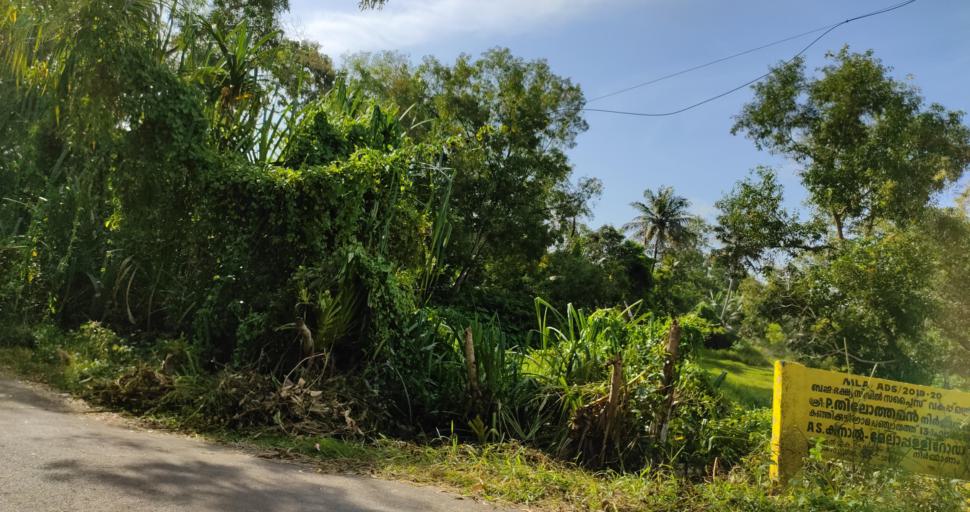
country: IN
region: Kerala
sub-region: Alappuzha
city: Shertallai
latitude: 9.6033
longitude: 76.3336
